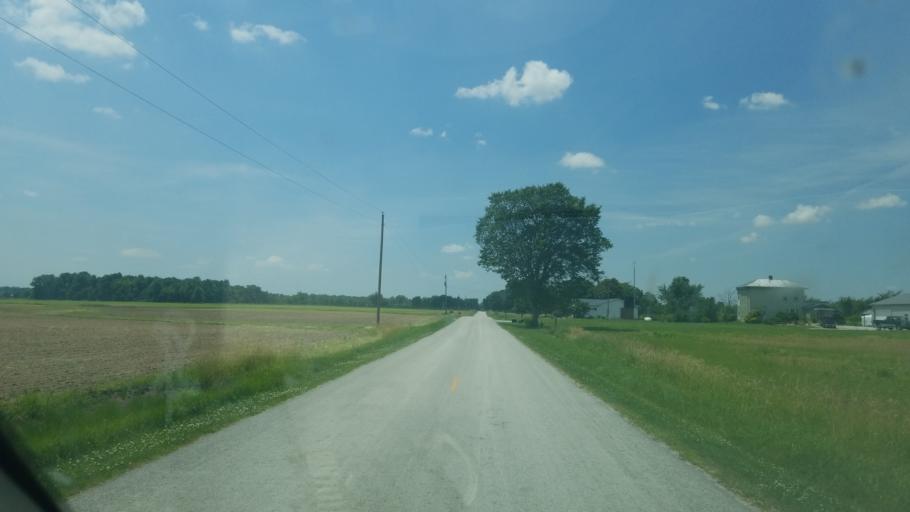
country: US
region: Ohio
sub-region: Hardin County
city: Forest
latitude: 40.7897
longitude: -83.6162
